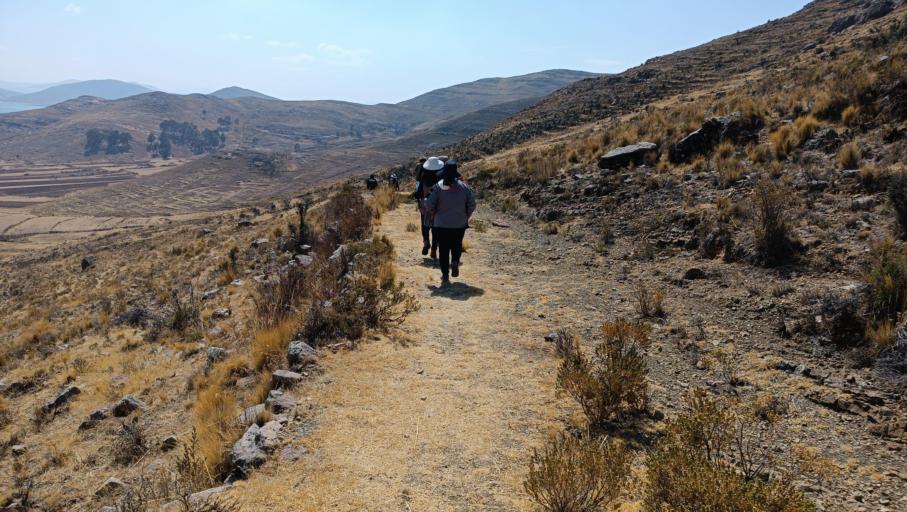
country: BO
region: La Paz
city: Batallas
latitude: -16.3497
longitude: -68.6545
